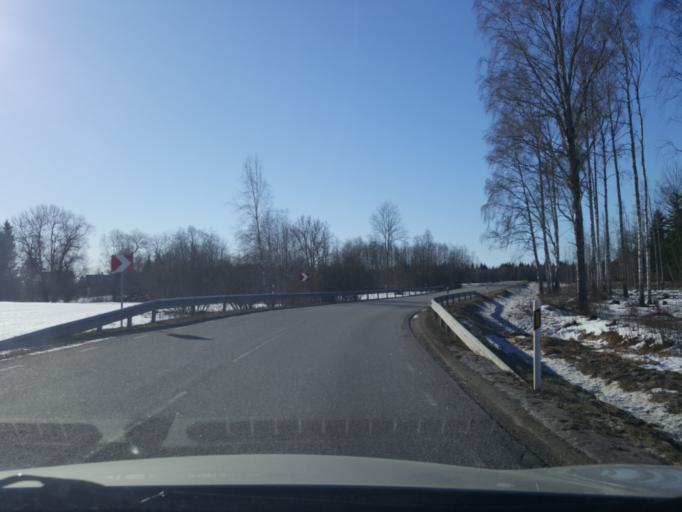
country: EE
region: Viljandimaa
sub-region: Viiratsi vald
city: Viiratsi
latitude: 58.4224
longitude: 25.6814
